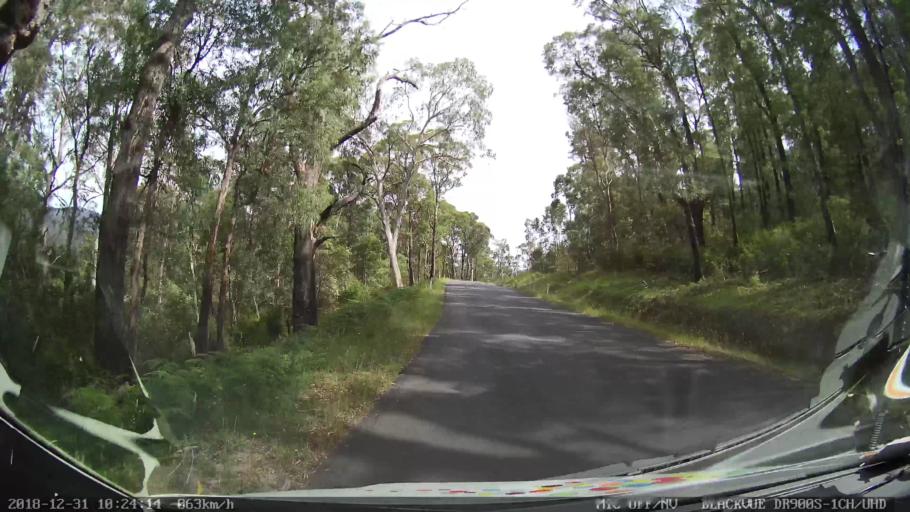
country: AU
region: New South Wales
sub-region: Snowy River
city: Jindabyne
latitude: -36.5138
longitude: 148.1403
